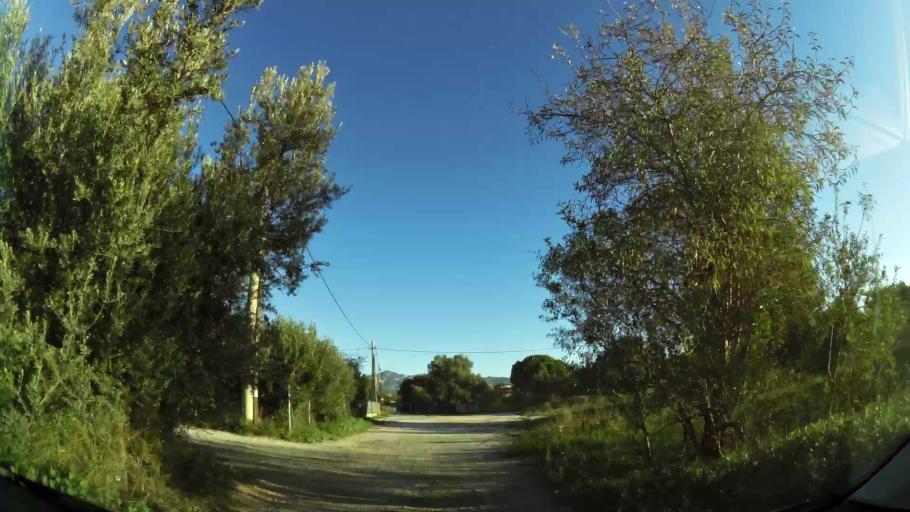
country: GR
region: Attica
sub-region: Nomarchia Anatolikis Attikis
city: Pallini
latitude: 37.9993
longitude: 23.8682
